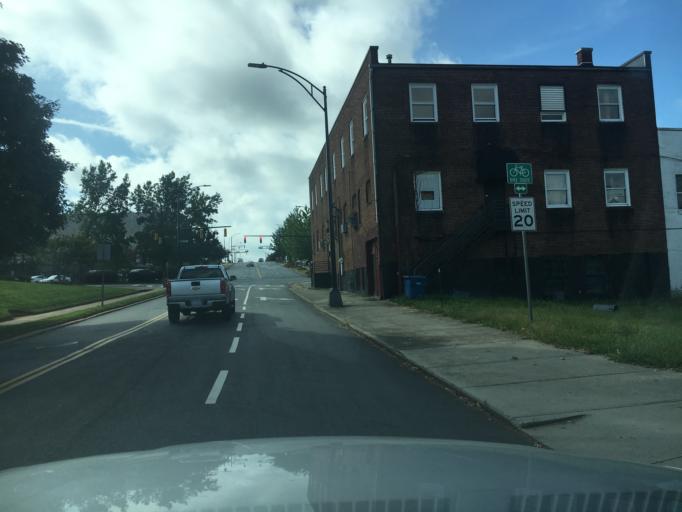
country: US
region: North Carolina
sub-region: Catawba County
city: Hickory
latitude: 35.7340
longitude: -81.3379
